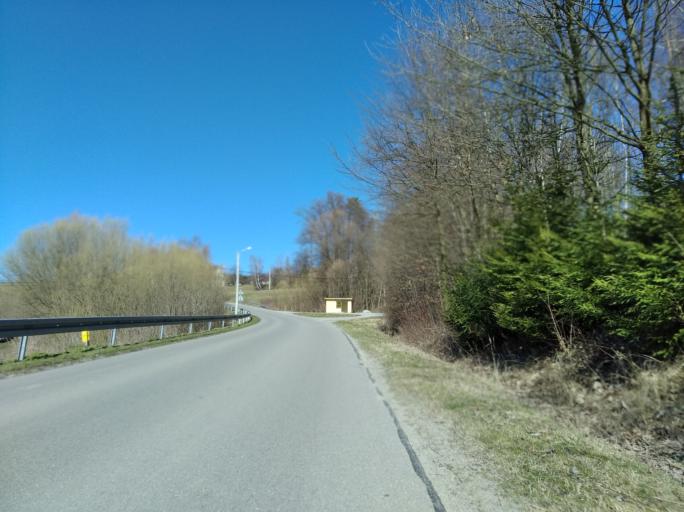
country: PL
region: Subcarpathian Voivodeship
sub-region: Powiat strzyzowski
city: Wisniowa
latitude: 49.8952
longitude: 21.6653
